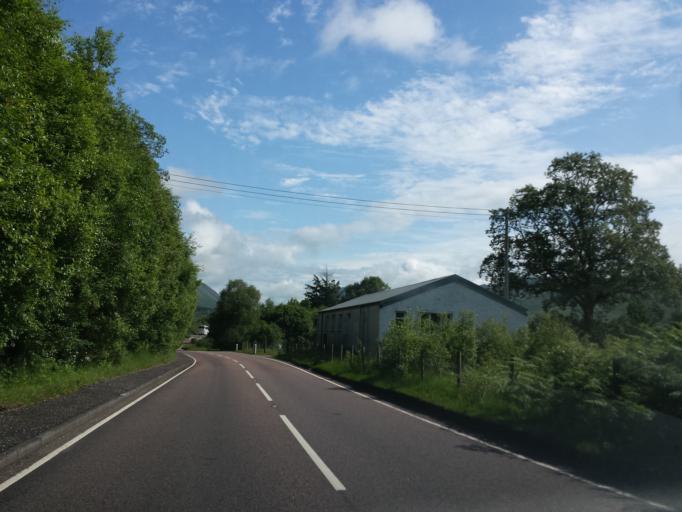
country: GB
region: Scotland
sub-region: Argyll and Bute
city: Garelochhead
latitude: 56.4078
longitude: -5.0323
